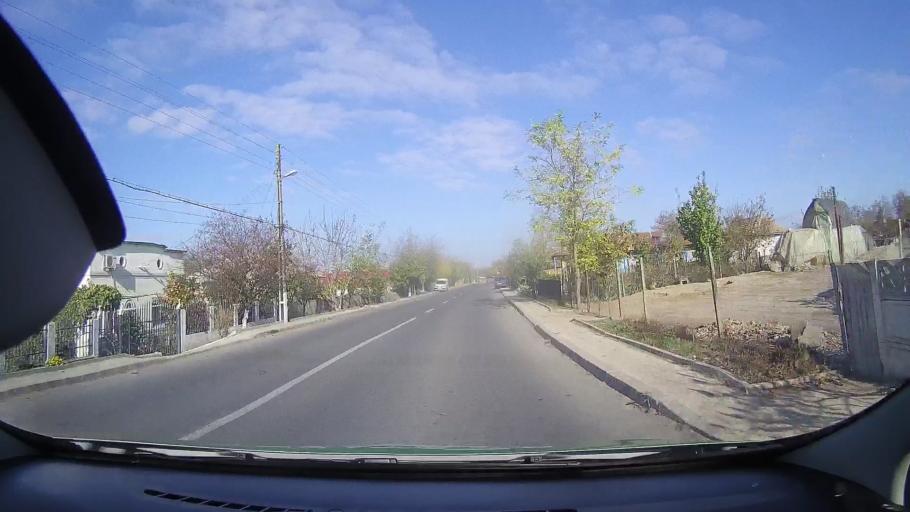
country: RO
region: Tulcea
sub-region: Comuna Valea Nucarilor
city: Valea Nucarilor
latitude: 45.0373
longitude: 28.9404
